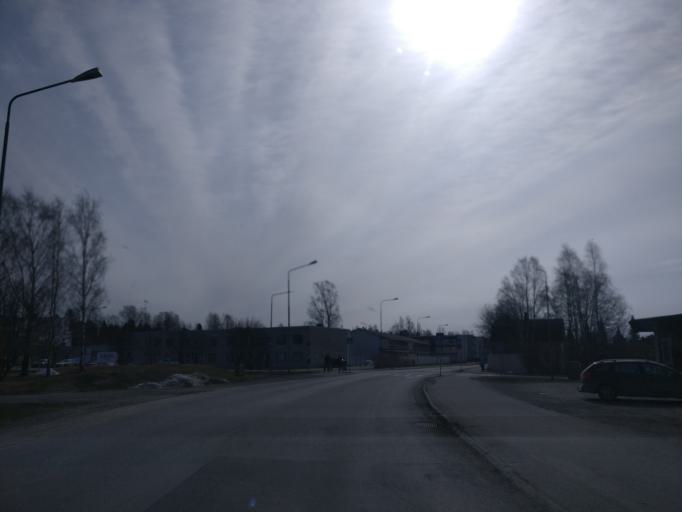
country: FI
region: Lapland
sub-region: Kemi-Tornio
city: Kemi
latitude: 65.7502
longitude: 24.5602
